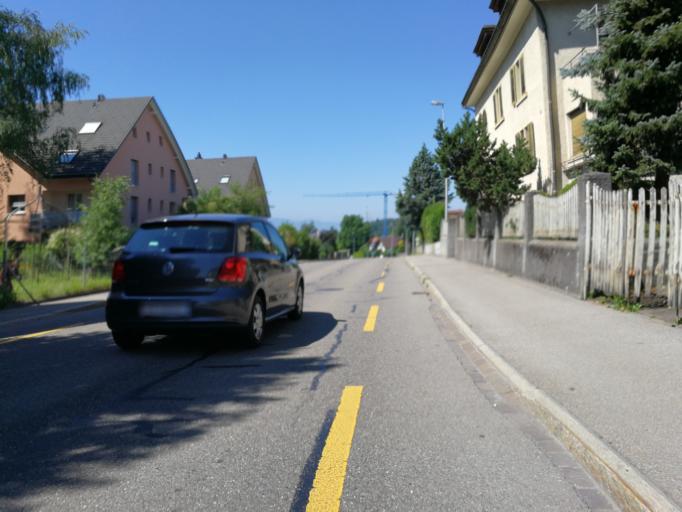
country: CH
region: Zurich
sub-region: Bezirk Hinwil
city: Bubikon
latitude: 47.2679
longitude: 8.8182
